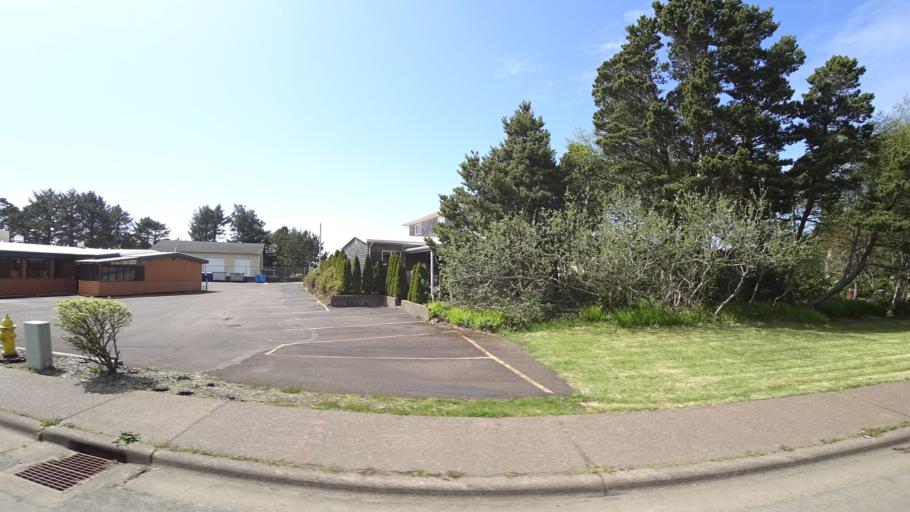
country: US
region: Oregon
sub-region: Lincoln County
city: Lincoln Beach
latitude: 44.8433
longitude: -124.0482
